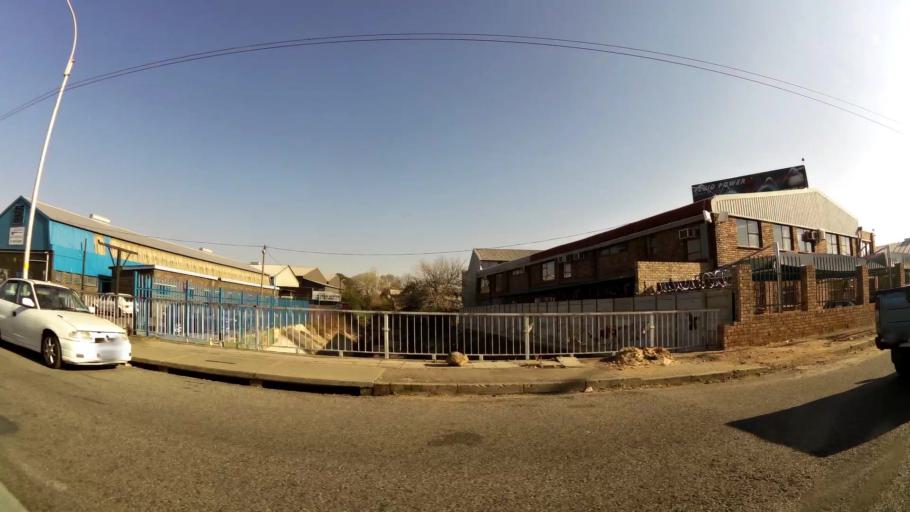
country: ZA
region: Gauteng
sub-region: City of Johannesburg Metropolitan Municipality
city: Modderfontein
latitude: -26.1316
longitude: 28.1583
